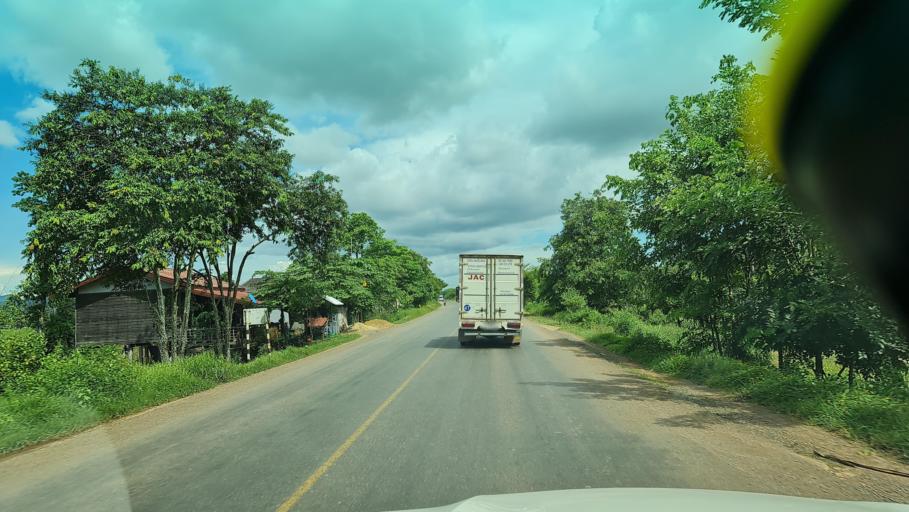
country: LA
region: Bolikhamxai
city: Ban Nahin
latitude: 18.1896
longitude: 104.2231
